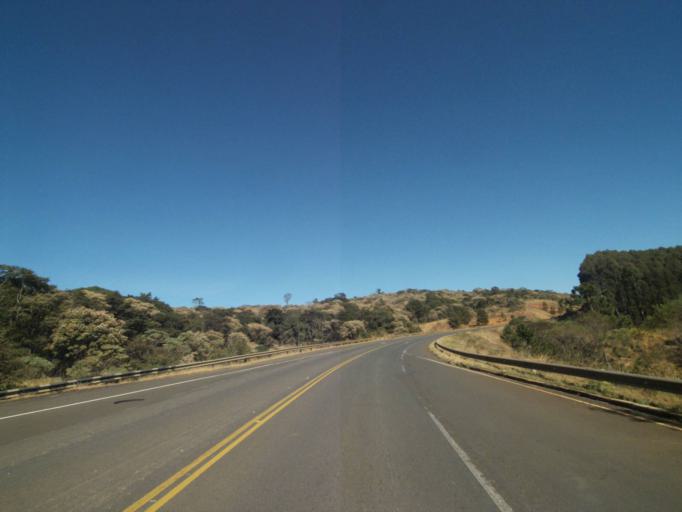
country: BR
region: Parana
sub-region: Tibagi
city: Tibagi
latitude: -24.4067
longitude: -50.3444
